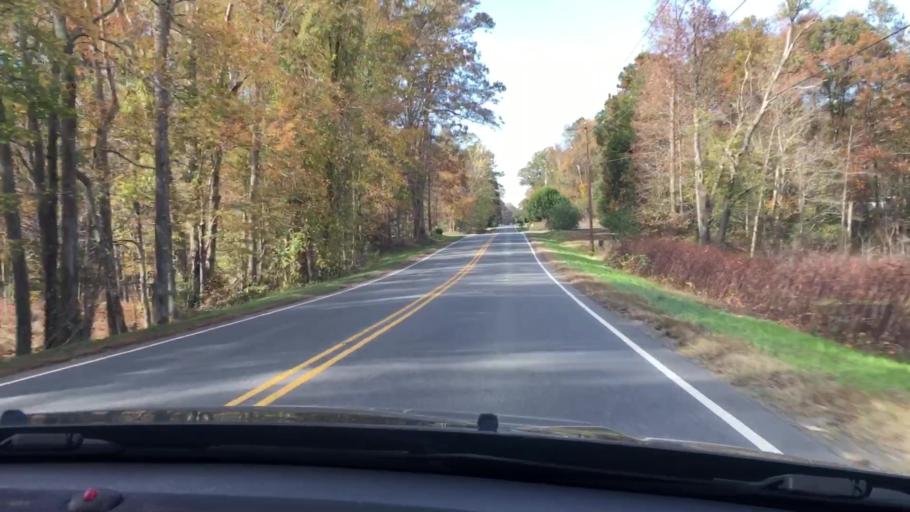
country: US
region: Virginia
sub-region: King William County
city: West Point
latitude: 37.5690
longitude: -76.8336
